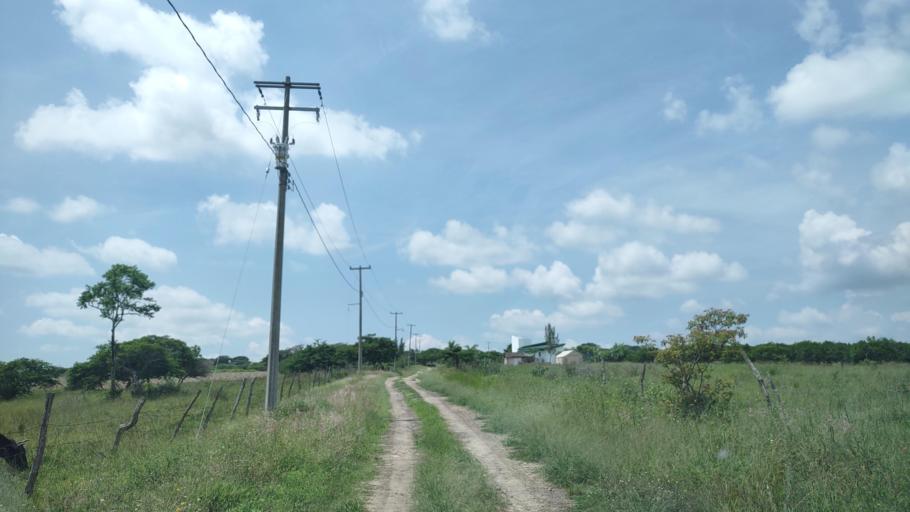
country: MX
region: Veracruz
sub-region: Emiliano Zapata
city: Dos Rios
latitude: 19.4665
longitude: -96.7961
